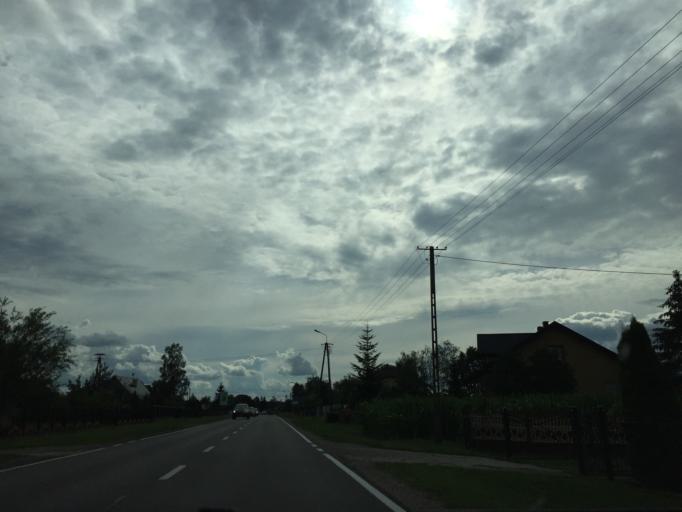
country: PL
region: Lublin Voivodeship
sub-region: Powiat lukowski
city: Lukow
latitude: 51.9503
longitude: 22.4453
